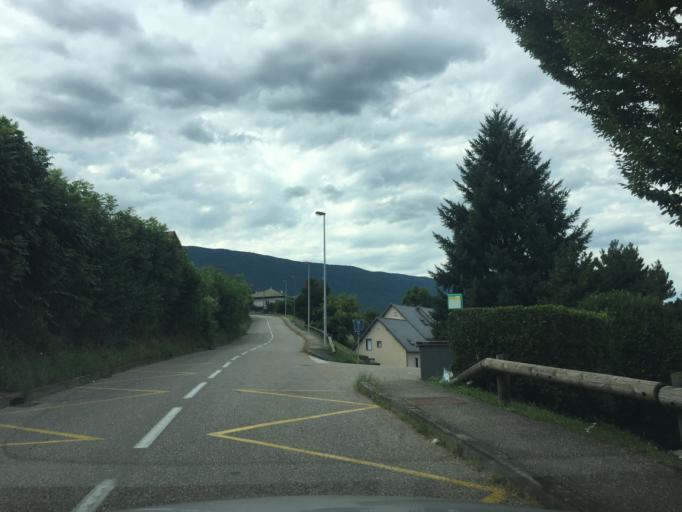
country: FR
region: Rhone-Alpes
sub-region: Departement de la Savoie
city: La Motte-Servolex
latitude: 45.5847
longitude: 5.8818
